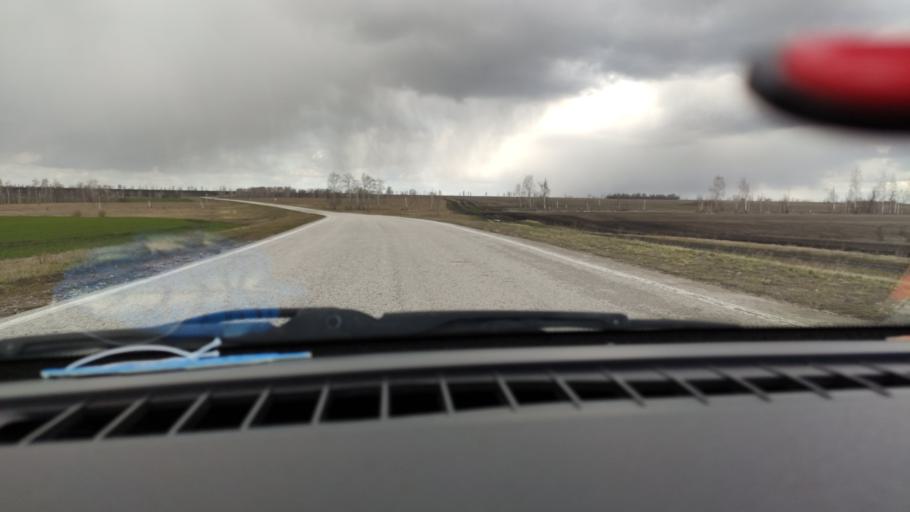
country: RU
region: Samara
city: Povolzhskiy
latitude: 53.7923
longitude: 49.7213
